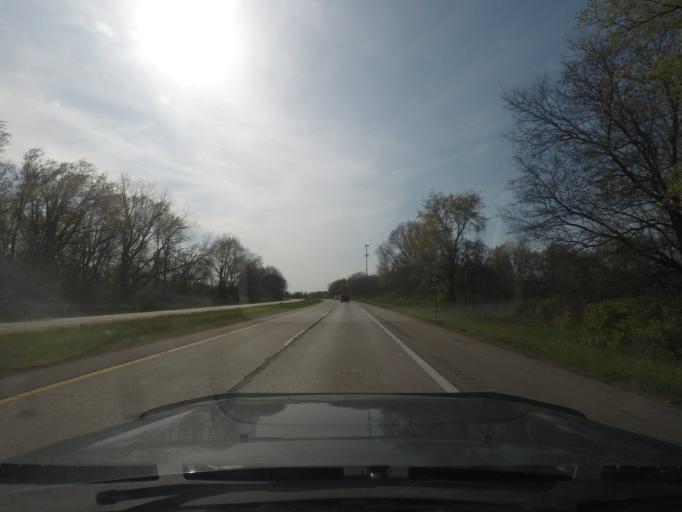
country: US
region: Michigan
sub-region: Berrien County
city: Niles
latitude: 41.8045
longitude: -86.2922
